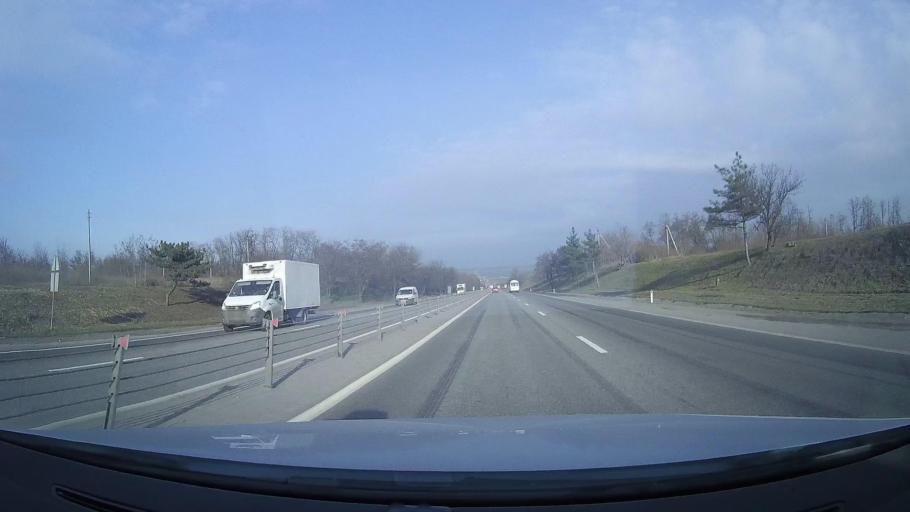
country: RU
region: Rostov
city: Grushevskaya
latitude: 47.4264
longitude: 39.9751
